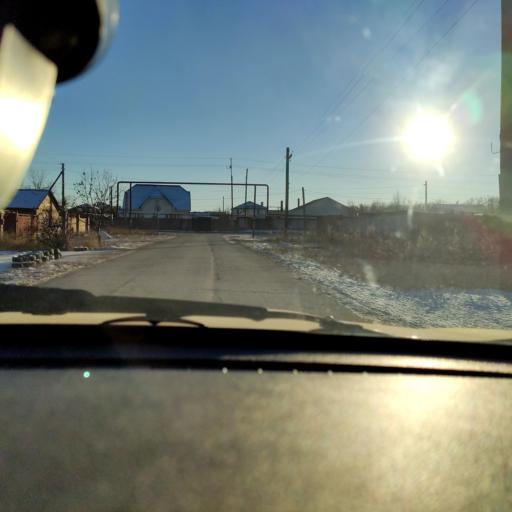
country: RU
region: Samara
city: Tol'yatti
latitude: 53.5565
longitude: 49.3975
